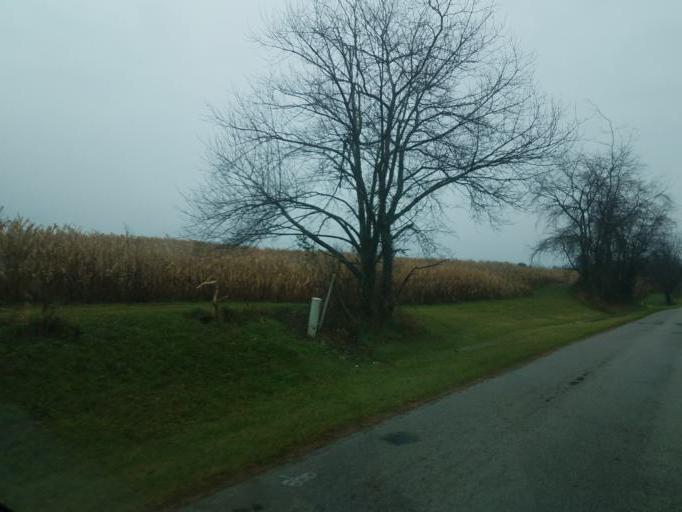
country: US
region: Ohio
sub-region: Knox County
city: Centerburg
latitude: 40.3631
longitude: -82.7055
